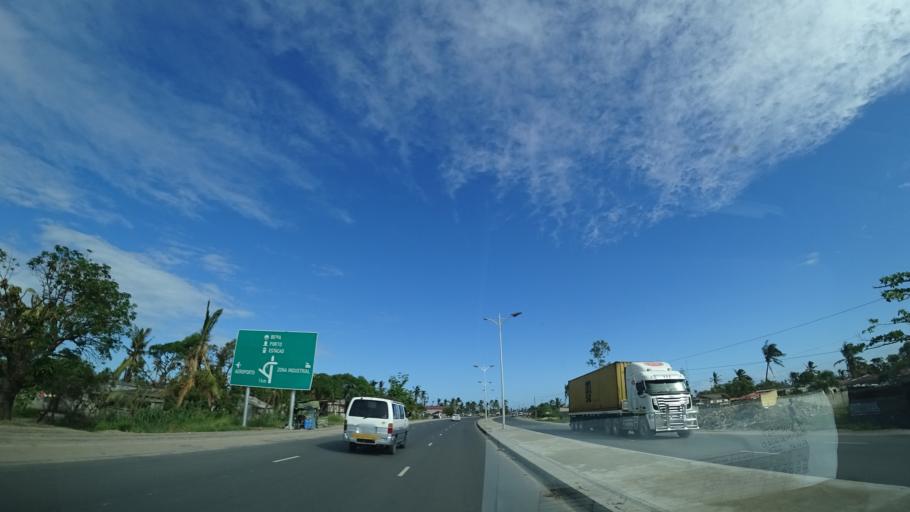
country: MZ
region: Sofala
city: Beira
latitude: -19.7723
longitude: 34.8834
